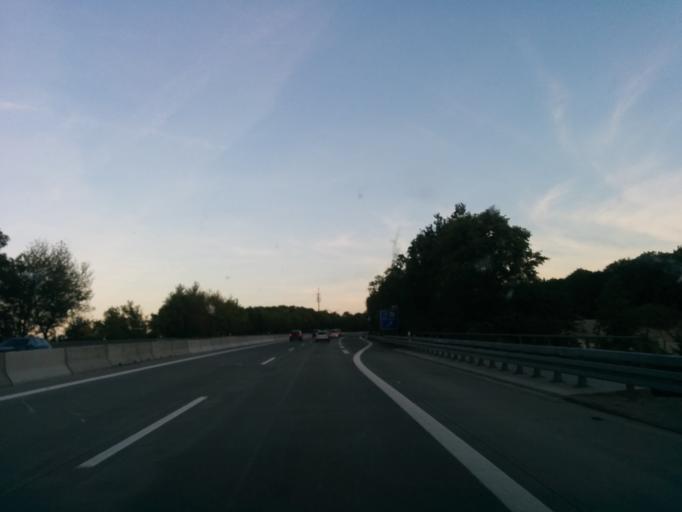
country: DE
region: Bavaria
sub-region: Regierungsbezirk Unterfranken
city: Martinsheim
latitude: 49.6303
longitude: 10.1762
